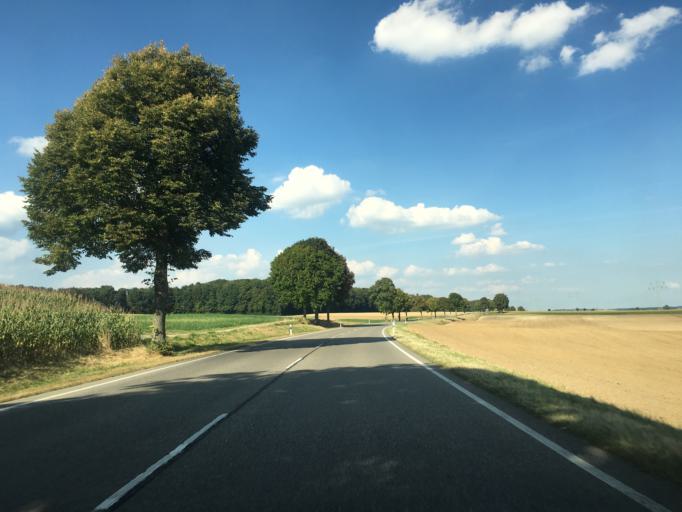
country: DE
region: Baden-Wuerttemberg
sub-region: Tuebingen Region
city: Rottenacker
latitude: 48.2661
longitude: 9.6723
